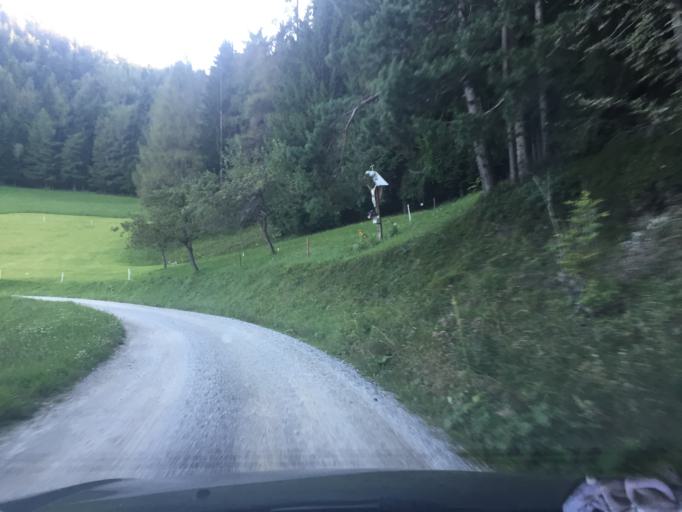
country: SI
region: Ravne na Koroskem
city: Kotlje
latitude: 46.4644
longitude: 14.9898
